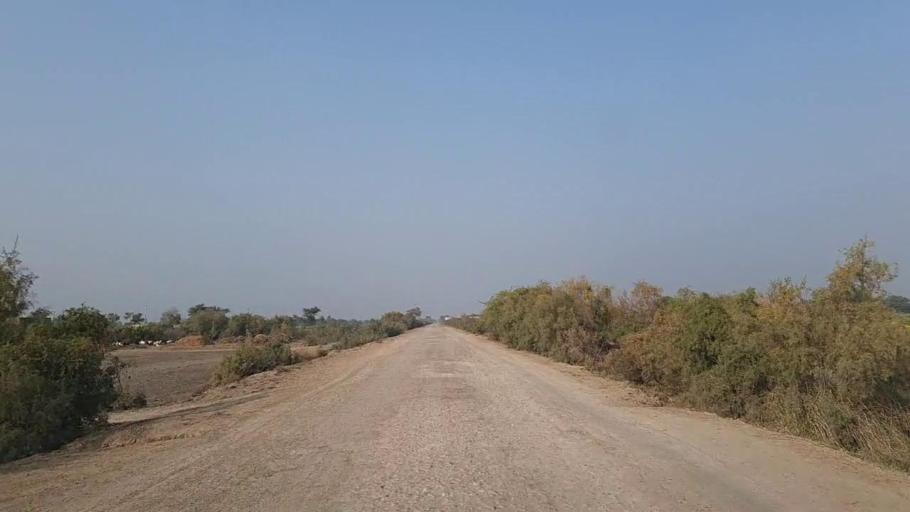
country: PK
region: Sindh
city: Nawabshah
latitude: 26.3346
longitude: 68.4891
